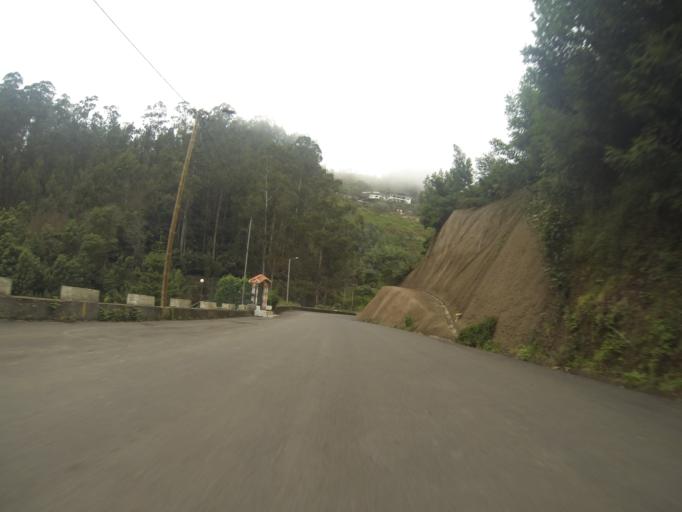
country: PT
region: Madeira
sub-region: Camara de Lobos
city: Curral das Freiras
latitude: 32.6849
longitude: -16.9540
